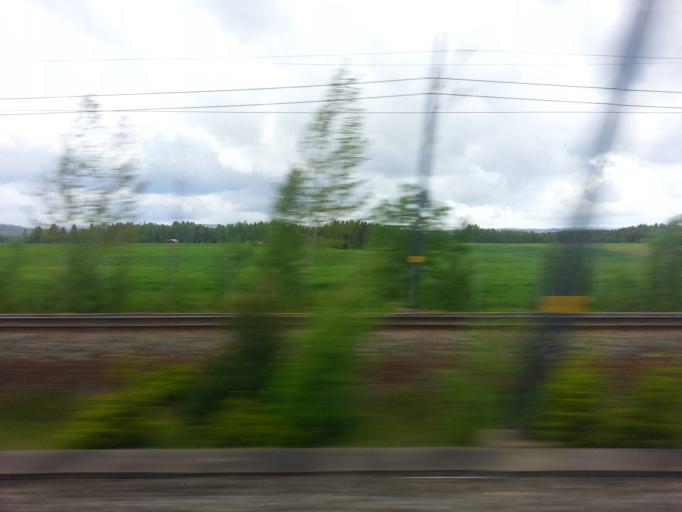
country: NO
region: Akershus
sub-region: Ullensaker
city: Klofta
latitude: 60.0585
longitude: 11.1396
